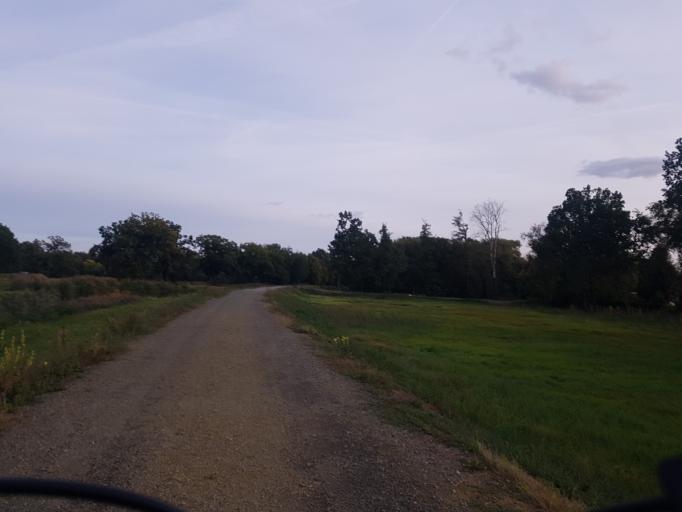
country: DE
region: Brandenburg
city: Bad Liebenwerda
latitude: 51.5532
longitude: 13.3653
